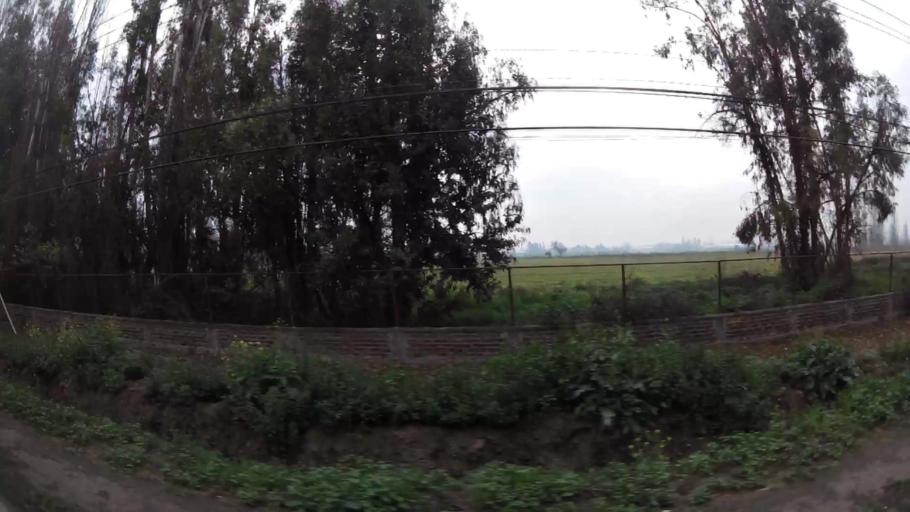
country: CL
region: Santiago Metropolitan
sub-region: Provincia de Chacabuco
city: Chicureo Abajo
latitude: -33.2450
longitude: -70.7647
